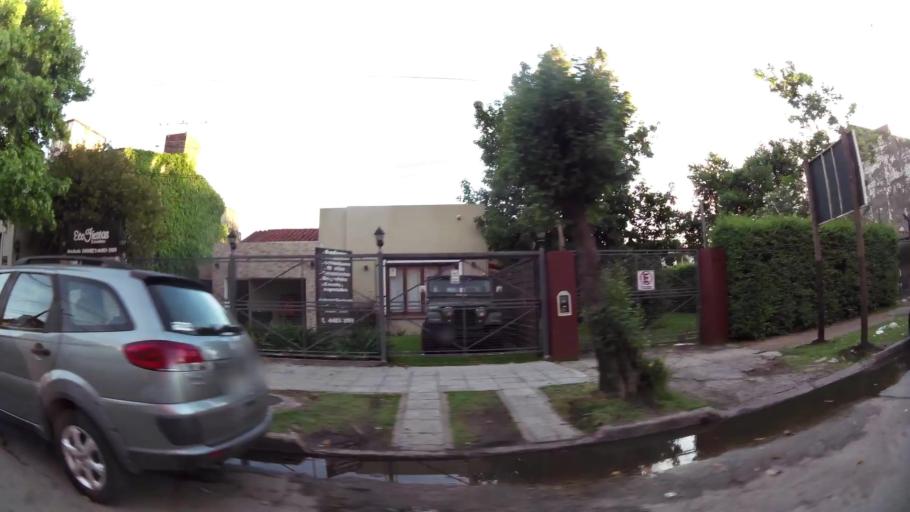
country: AR
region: Buenos Aires
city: Ituzaingo
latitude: -34.6485
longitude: -58.6430
